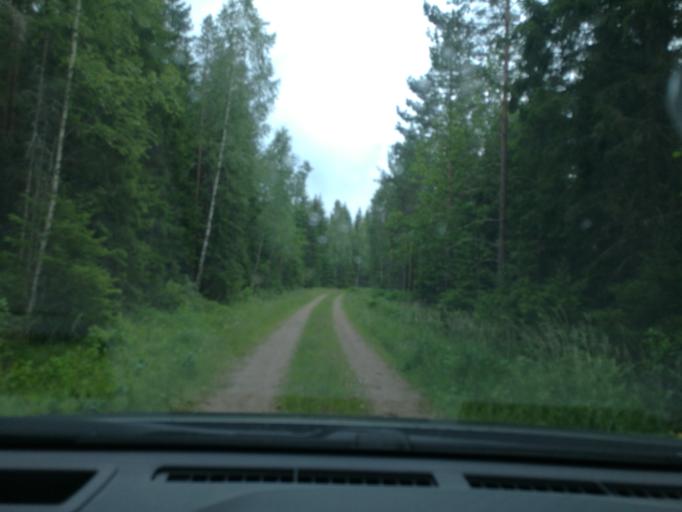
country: SE
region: Vaestmanland
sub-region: Surahammars Kommun
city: Ramnas
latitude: 59.8087
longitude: 16.3206
